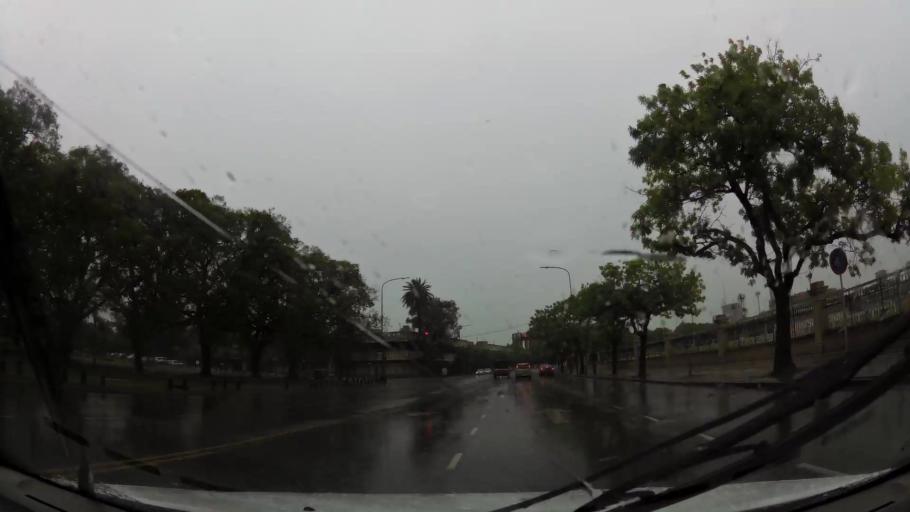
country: AR
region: Buenos Aires F.D.
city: Colegiales
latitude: -34.5681
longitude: -58.4216
